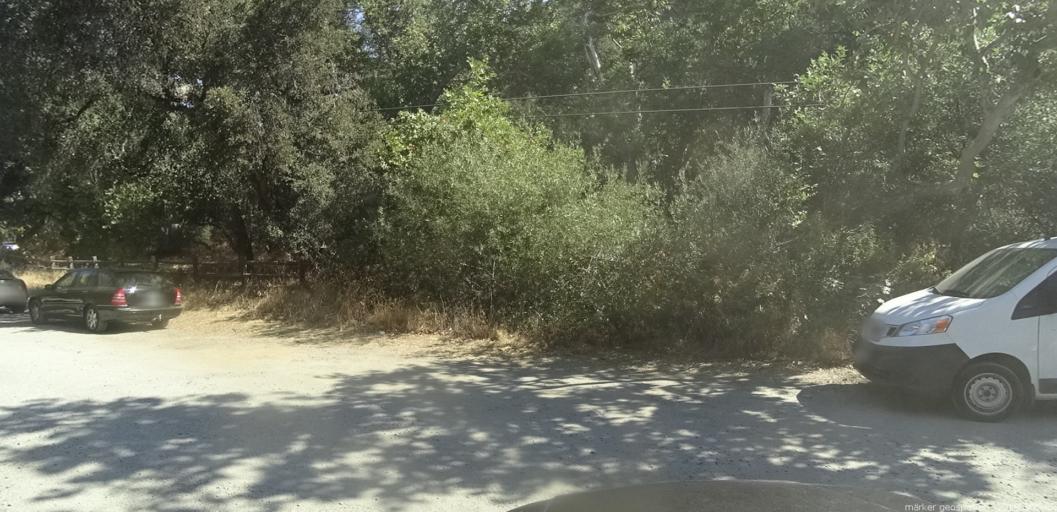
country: US
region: California
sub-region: Monterey County
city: Gonzales
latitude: 36.3690
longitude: -121.5903
